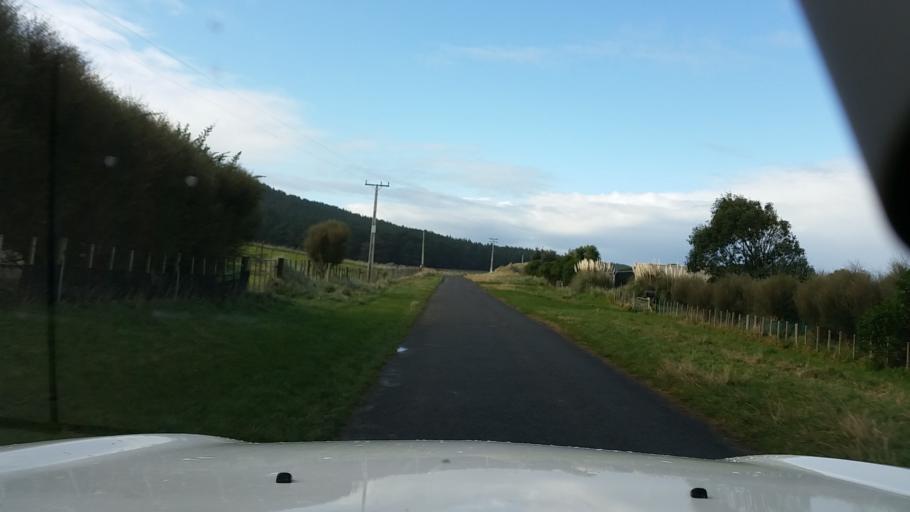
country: NZ
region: Wellington
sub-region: Masterton District
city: Masterton
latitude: -41.2456
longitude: 175.9377
